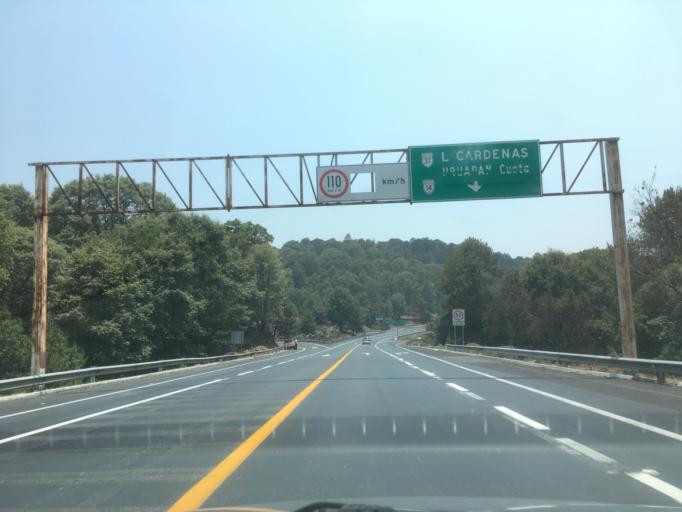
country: MX
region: Michoacan
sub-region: Patzcuaro
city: Santa Maria Huiramangaro (San Juan Tumbio)
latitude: 19.4833
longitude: -101.7260
